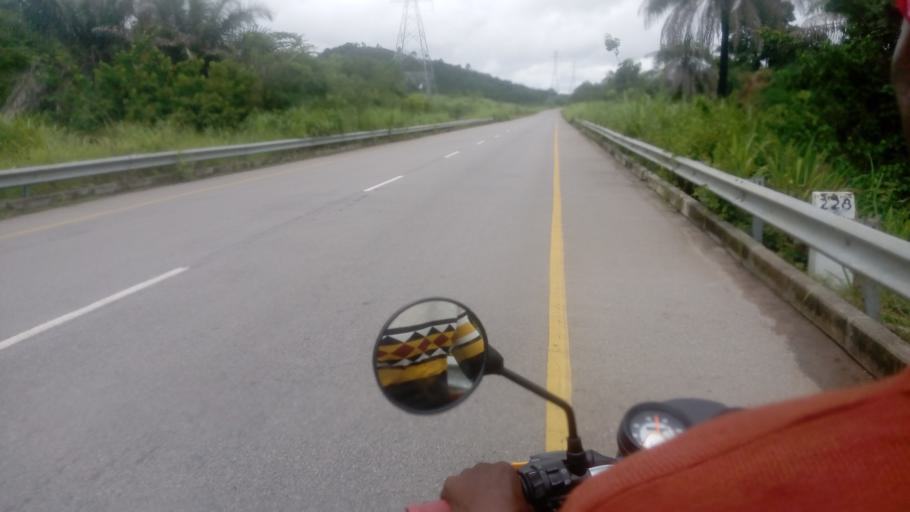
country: SL
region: Northern Province
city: Masaka
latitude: 8.6493
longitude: -11.7673
